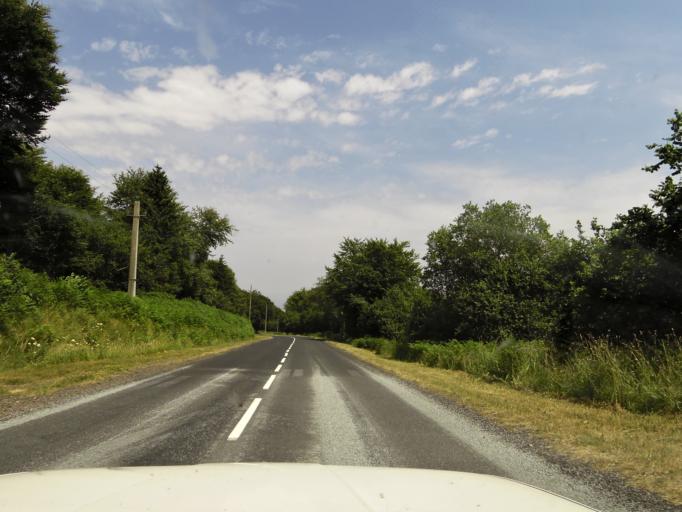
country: FR
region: Auvergne
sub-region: Departement du Puy-de-Dome
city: Orcines
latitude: 45.7640
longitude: 2.9659
